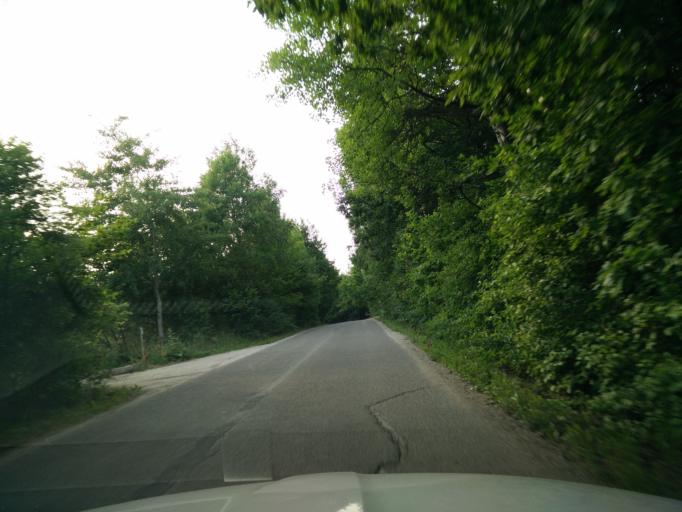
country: SK
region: Nitriansky
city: Prievidza
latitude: 48.7383
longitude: 18.6361
